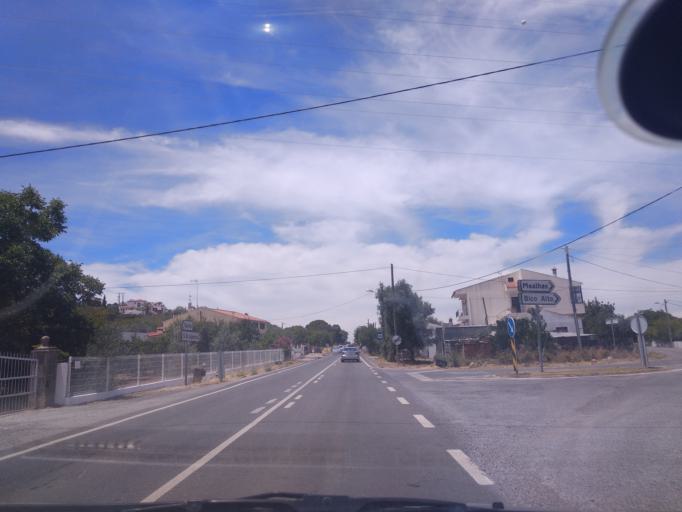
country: PT
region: Faro
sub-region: Sao Bras de Alportel
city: Sao Bras de Alportel
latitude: 37.1547
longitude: -7.8604
